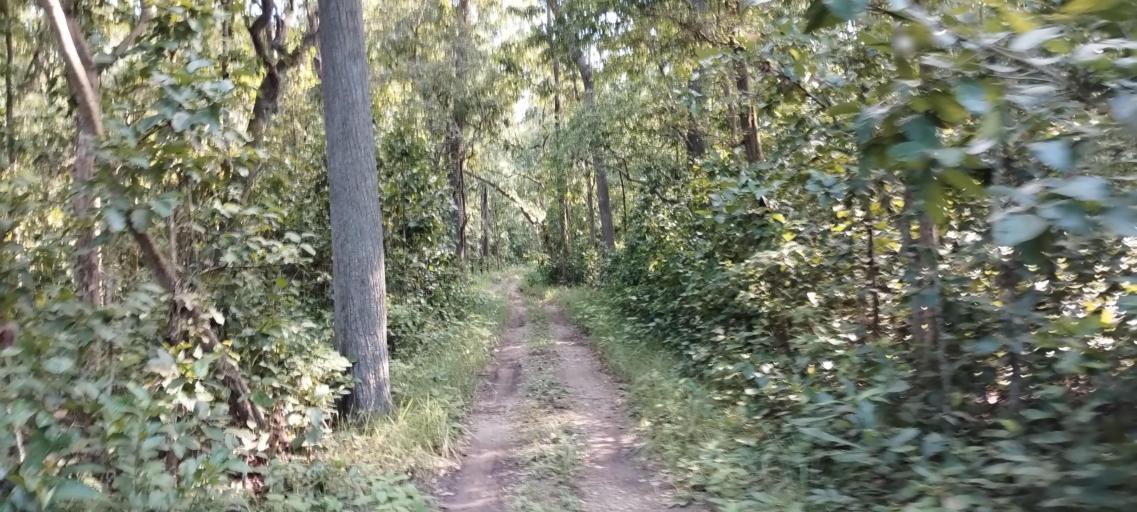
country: NP
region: Far Western
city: Tikapur
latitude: 28.5399
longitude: 81.2864
